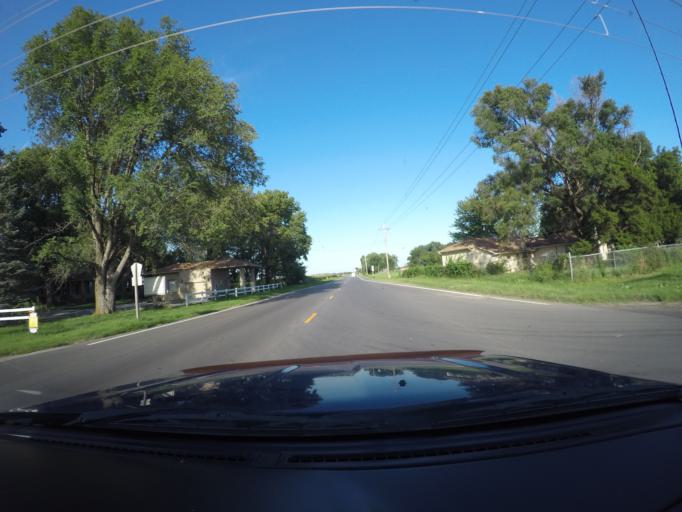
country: US
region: Kansas
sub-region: Douglas County
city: Lawrence
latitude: 39.0005
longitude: -95.2240
